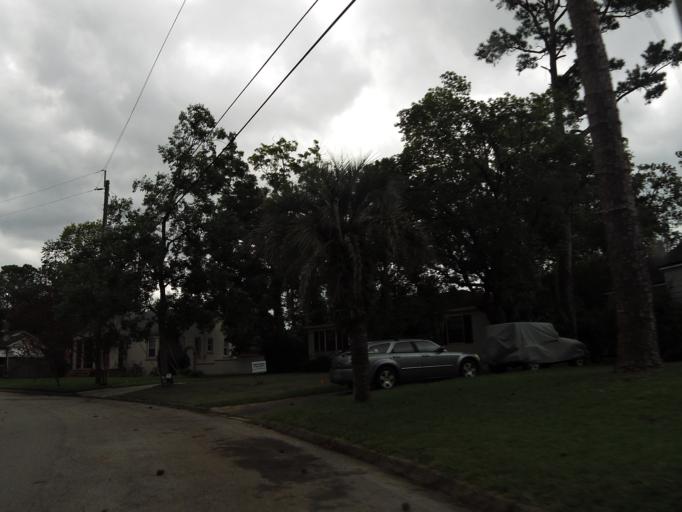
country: US
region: Florida
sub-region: Duval County
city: Jacksonville
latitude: 30.3011
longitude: -81.6370
